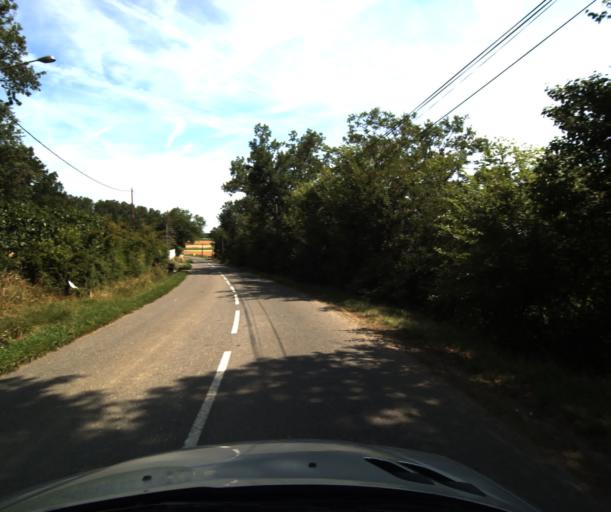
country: FR
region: Midi-Pyrenees
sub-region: Departement de la Haute-Garonne
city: Labastidette
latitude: 43.4718
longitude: 1.2173
